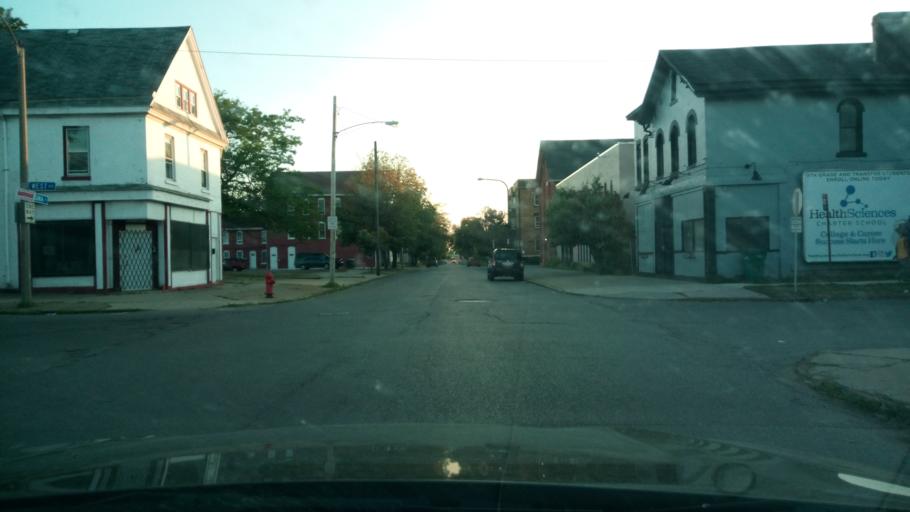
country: US
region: New York
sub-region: Erie County
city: Buffalo
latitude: 42.8953
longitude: -78.8811
